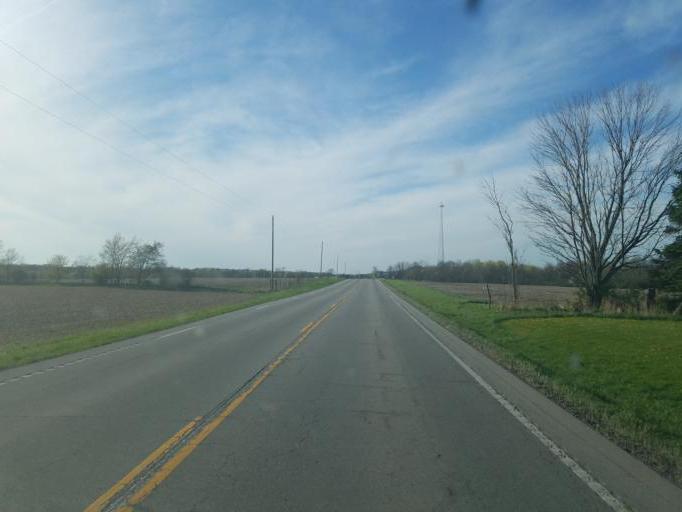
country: US
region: Ohio
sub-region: Huron County
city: New London
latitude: 41.0204
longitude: -82.4120
